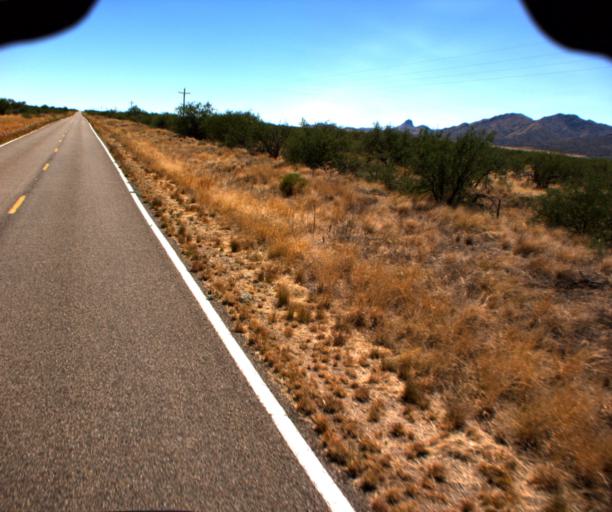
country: US
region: Arizona
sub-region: Pima County
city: Three Points
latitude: 31.7754
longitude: -111.4646
